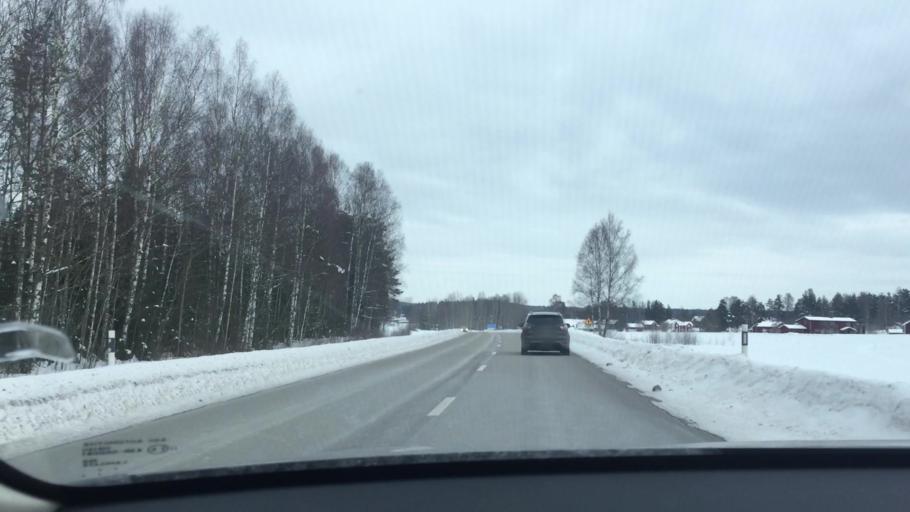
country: SE
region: Dalarna
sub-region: Faluns Kommun
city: Svardsjo
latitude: 60.6407
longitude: 15.8405
